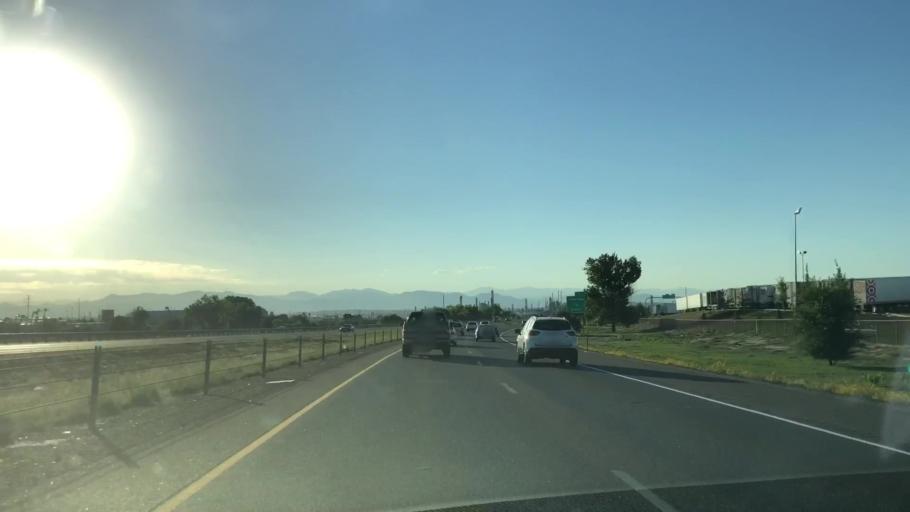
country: US
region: Colorado
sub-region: Adams County
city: Commerce City
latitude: 39.7955
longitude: -104.9246
